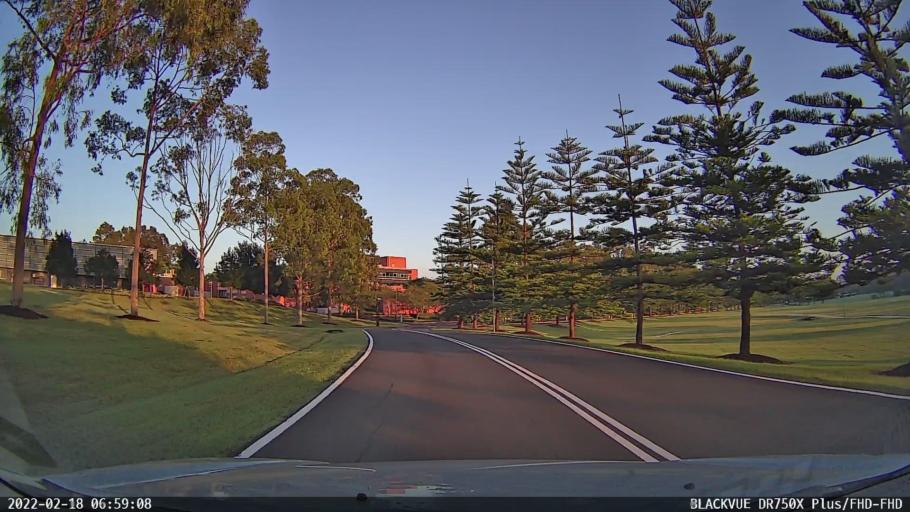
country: AU
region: New South Wales
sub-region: Penrith Municipality
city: Kingswood Park
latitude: -33.7695
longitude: 150.7307
